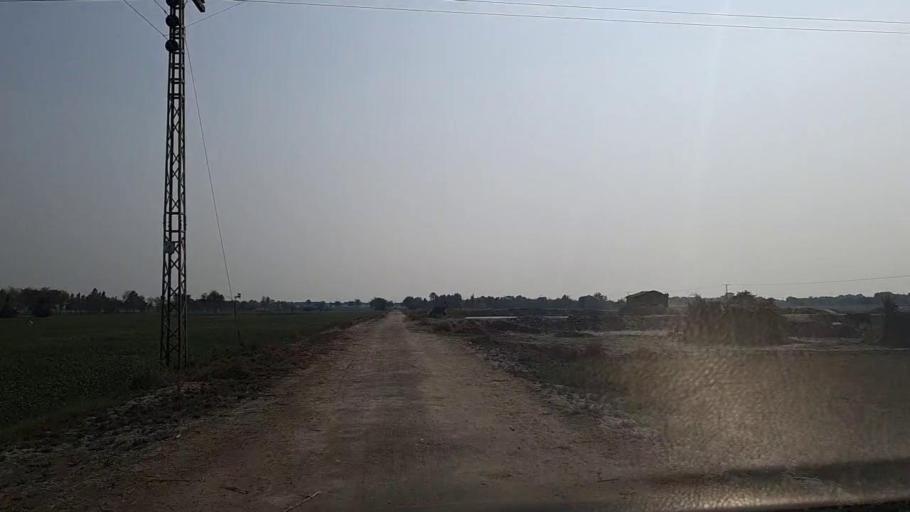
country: PK
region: Sindh
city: Daur
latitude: 26.4040
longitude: 68.4201
